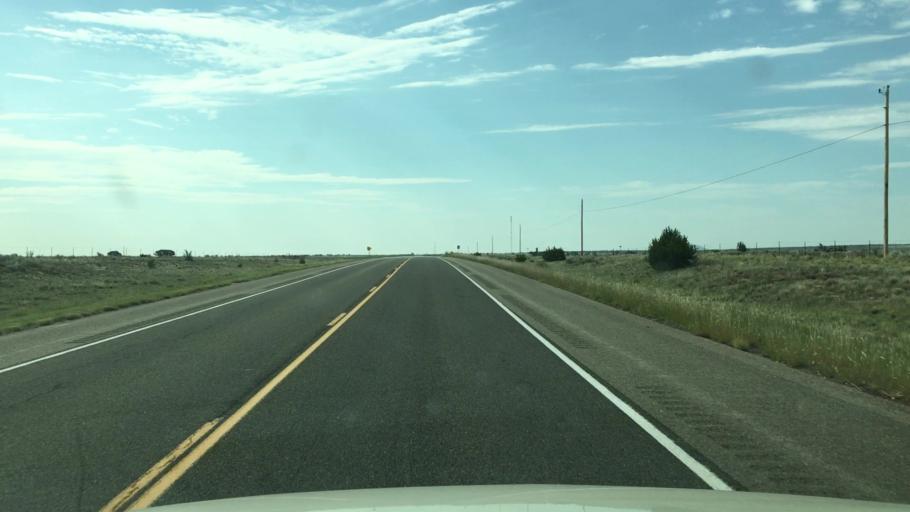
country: US
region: New Mexico
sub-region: Torrance County
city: Moriarty
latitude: 35.0283
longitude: -105.6755
